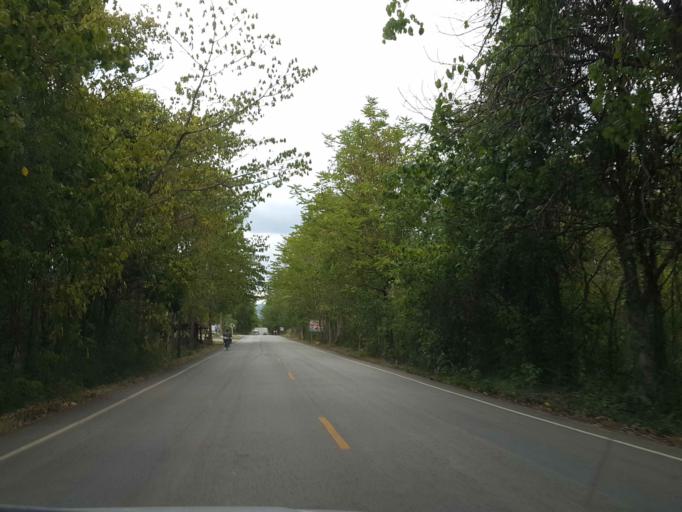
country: TH
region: Sukhothai
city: Thung Saliam
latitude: 17.3499
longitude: 99.4256
